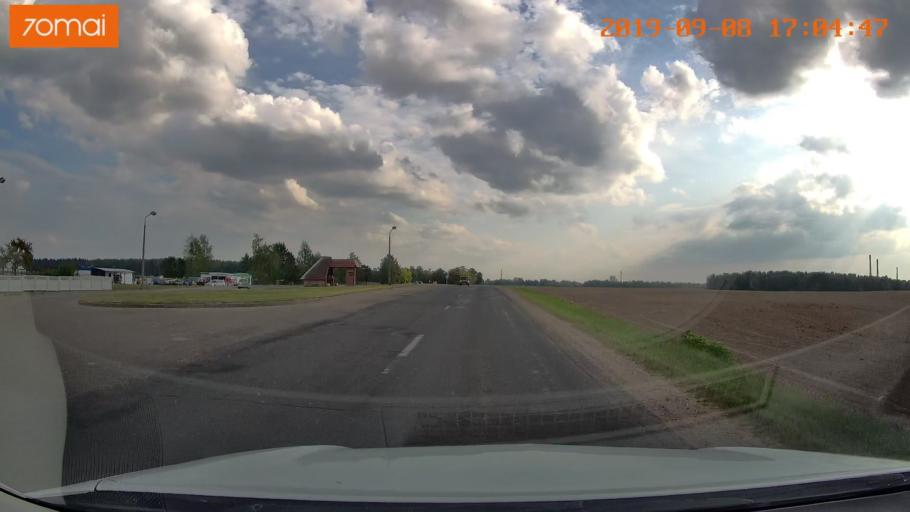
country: BY
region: Grodnenskaya
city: Hrodna
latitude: 53.6862
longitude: 23.9555
